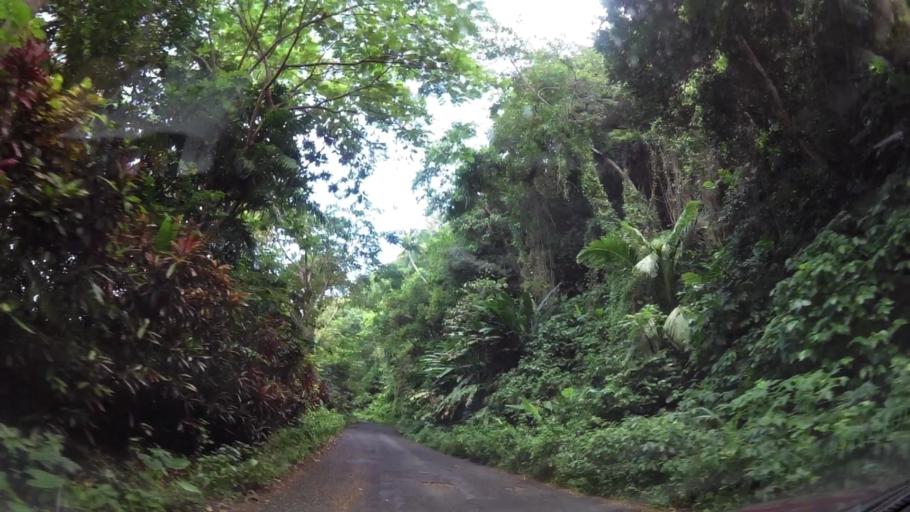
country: DM
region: Saint Andrew
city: Marigot
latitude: 15.5154
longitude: -61.2737
